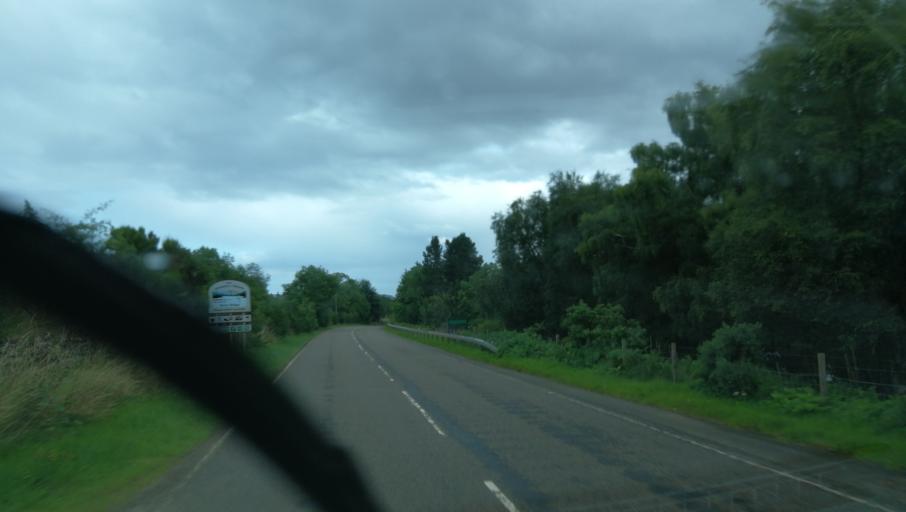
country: GB
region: Scotland
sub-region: Highland
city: Alness
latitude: 57.9015
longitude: -4.3547
